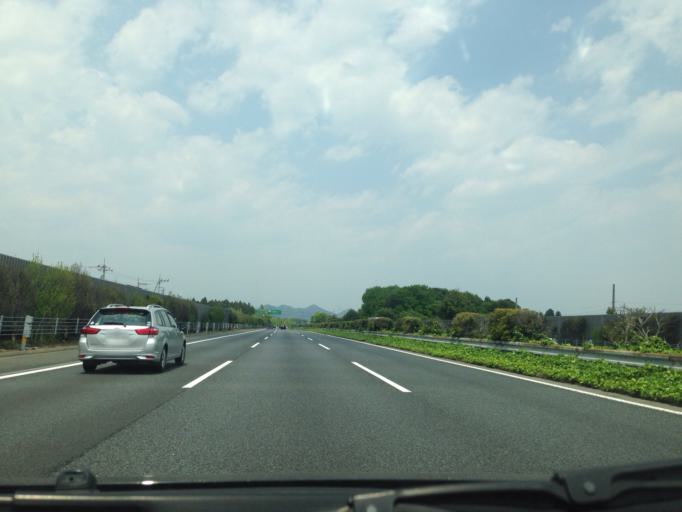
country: JP
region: Tochigi
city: Utsunomiya-shi
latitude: 36.6119
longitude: 139.8438
